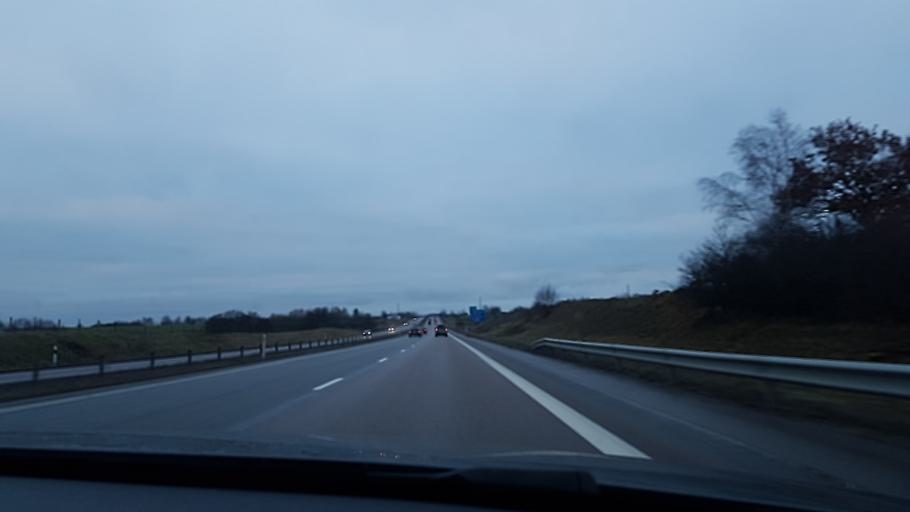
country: SE
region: Skane
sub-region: Astorps Kommun
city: Kvidinge
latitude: 56.1997
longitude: 13.0775
